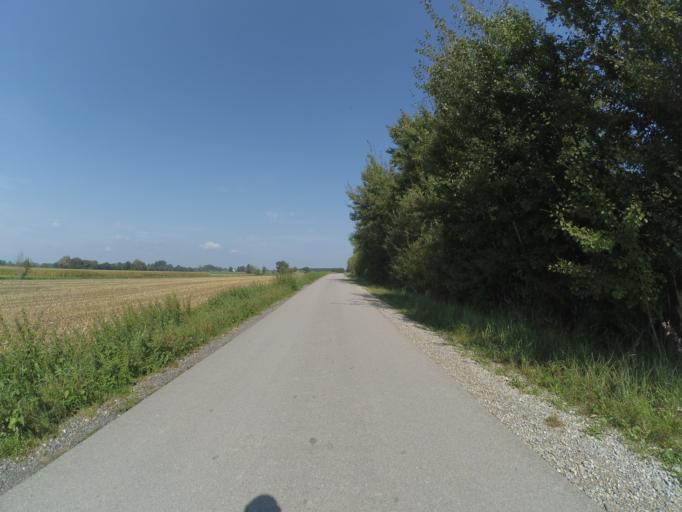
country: DE
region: Bavaria
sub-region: Swabia
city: Lamerdingen
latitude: 48.0668
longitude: 10.7281
